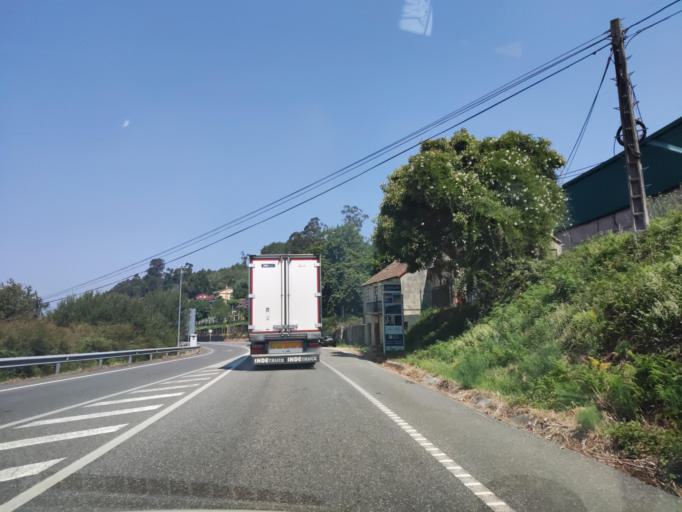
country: ES
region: Galicia
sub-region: Provincia de Pontevedra
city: Redondela
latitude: 42.2442
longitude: -8.5964
